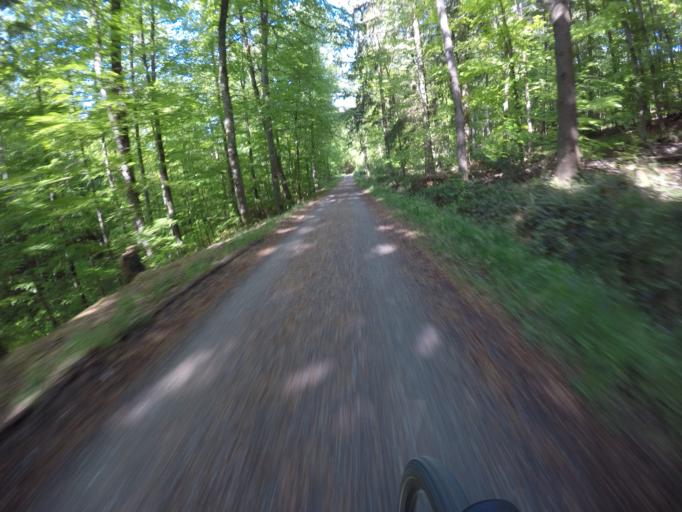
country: DE
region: Baden-Wuerttemberg
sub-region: Tuebingen Region
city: Dettenhausen
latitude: 48.5890
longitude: 9.1027
